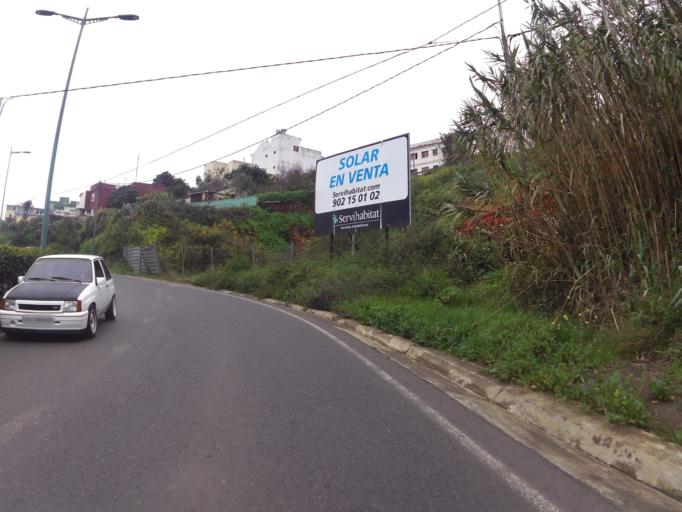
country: ES
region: Canary Islands
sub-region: Provincia de Las Palmas
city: Teror
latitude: 28.0626
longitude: -15.5403
